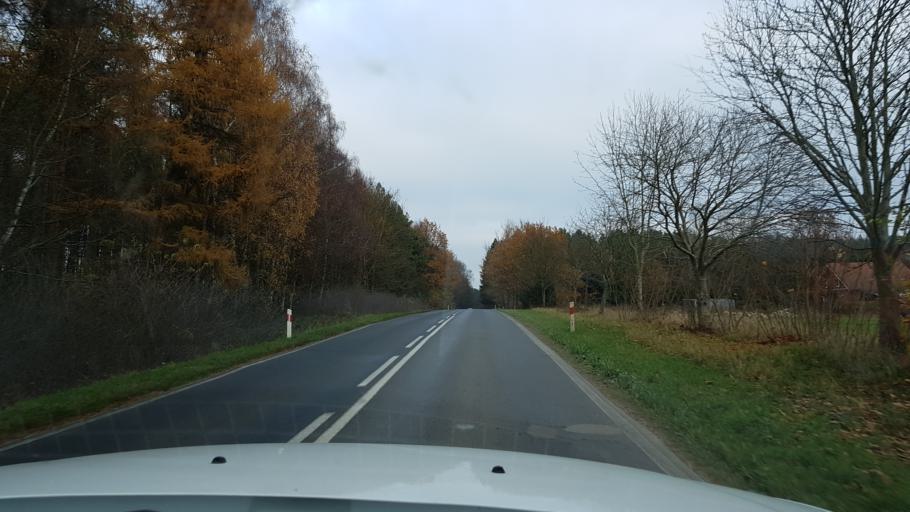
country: PL
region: West Pomeranian Voivodeship
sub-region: Powiat kolobrzeski
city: Grzybowo
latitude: 54.1097
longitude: 15.5278
